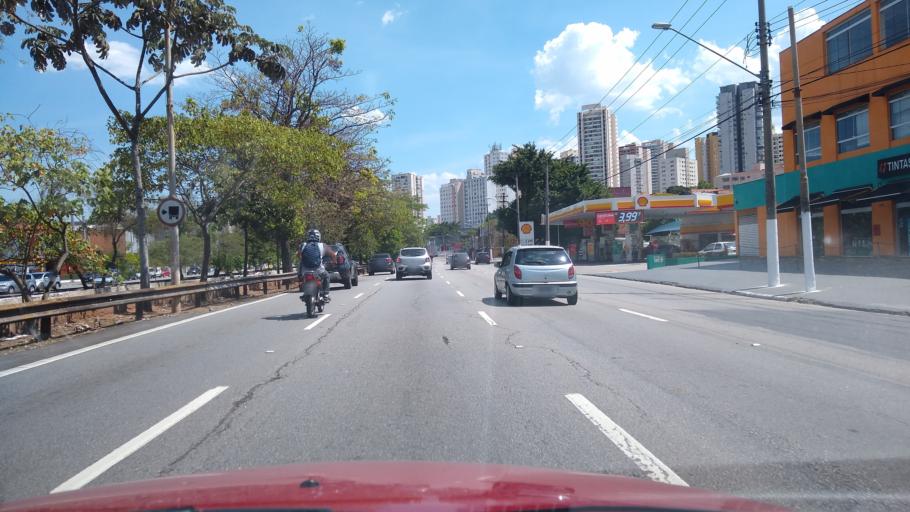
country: BR
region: Sao Paulo
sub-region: Sao Paulo
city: Sao Paulo
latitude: -23.6072
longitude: -46.6273
